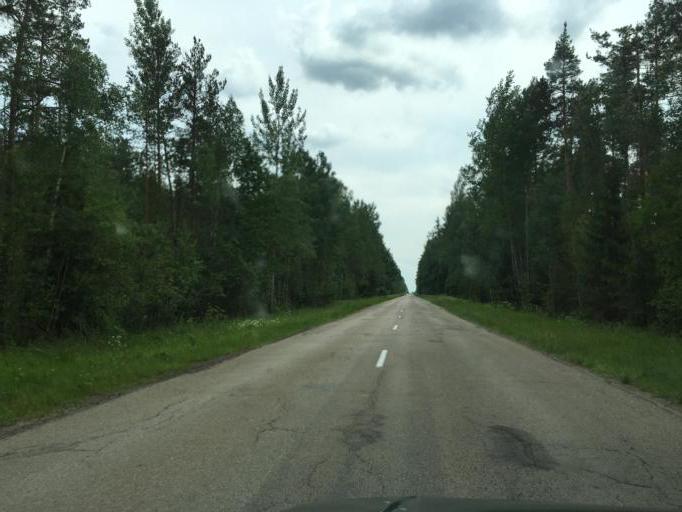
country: LV
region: Rugaju
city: Rugaji
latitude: 56.7841
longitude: 27.1031
